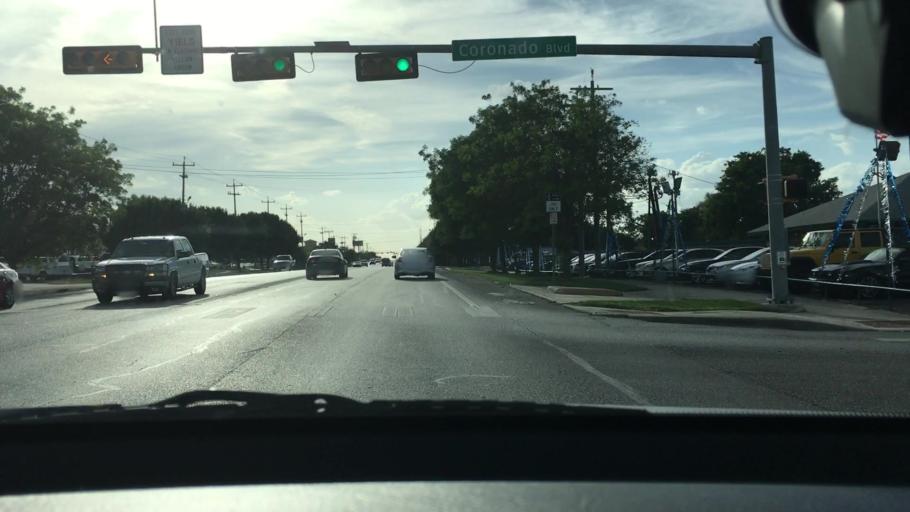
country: US
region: Texas
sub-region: Bexar County
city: Live Oak
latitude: 29.5560
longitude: -98.3160
